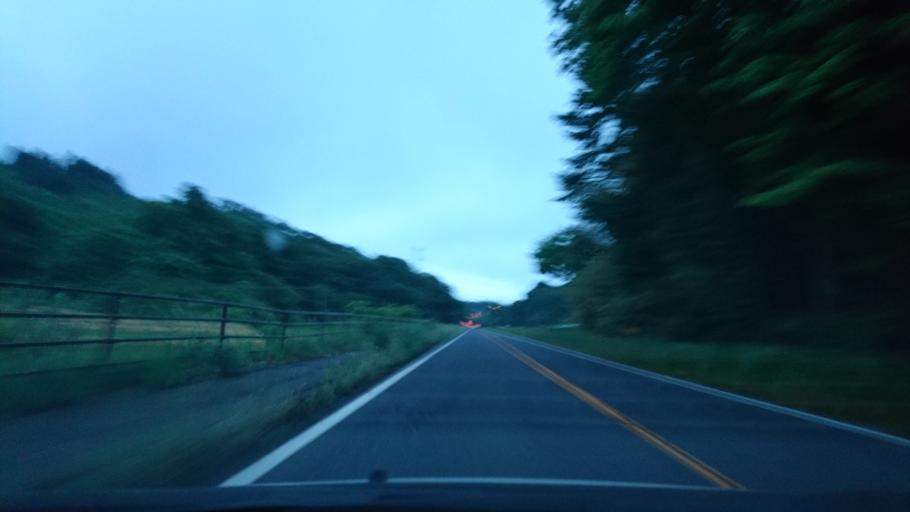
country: JP
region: Iwate
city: Ichinoseki
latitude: 38.8621
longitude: 141.1051
